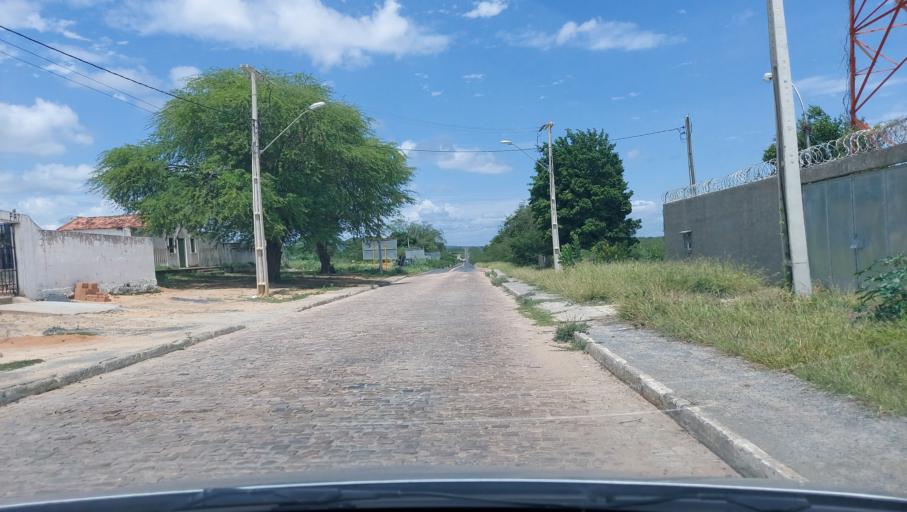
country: BR
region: Bahia
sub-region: Oliveira Dos Brejinhos
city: Beira Rio
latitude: -11.9946
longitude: -42.6303
